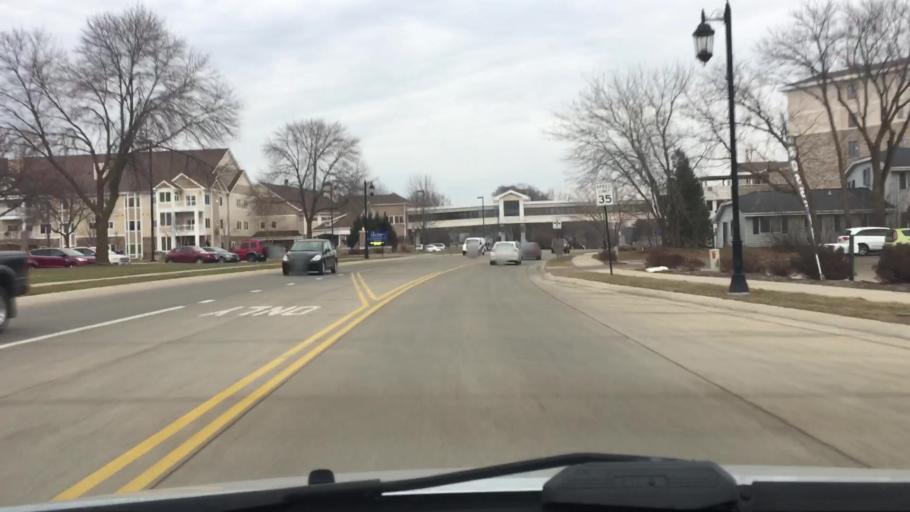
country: US
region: Wisconsin
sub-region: Waukesha County
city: Oconomowoc
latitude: 43.1210
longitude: -88.5227
